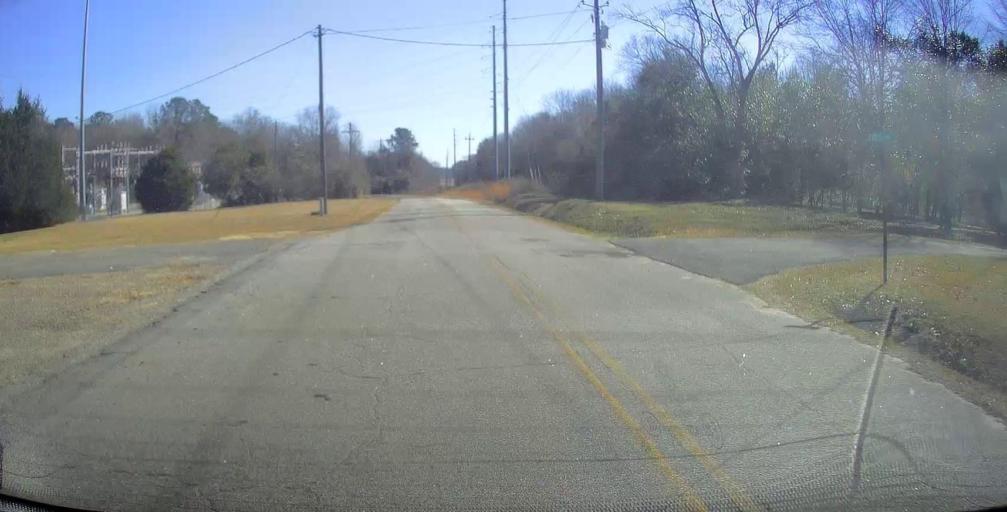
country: US
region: Georgia
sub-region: Crawford County
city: Roberta
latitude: 32.7179
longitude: -84.0093
